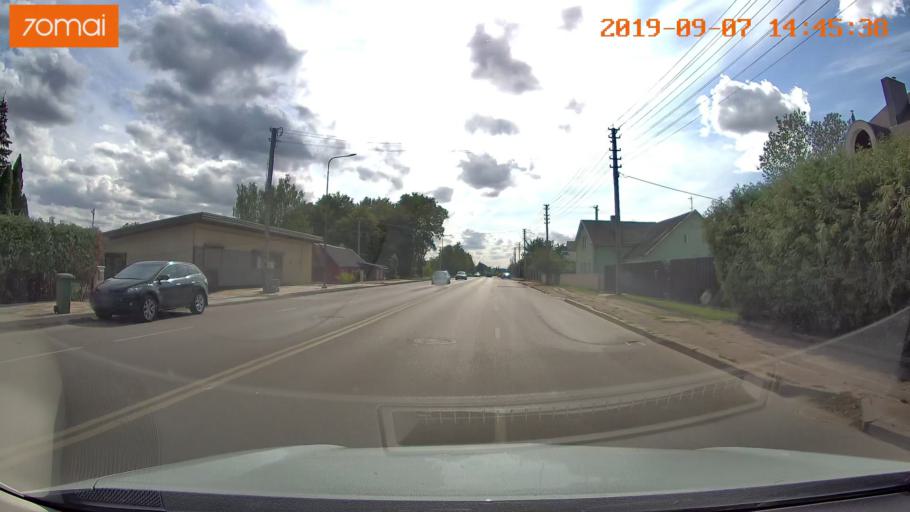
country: LT
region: Kauno apskritis
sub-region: Kaunas
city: Eiguliai
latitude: 54.9319
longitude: 23.9095
